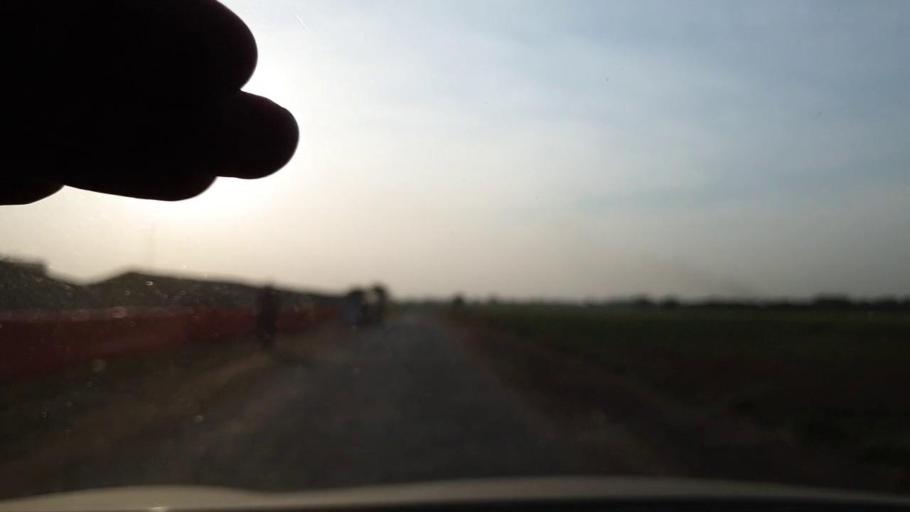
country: PK
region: Sindh
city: Tando Adam
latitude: 25.7086
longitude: 68.7289
